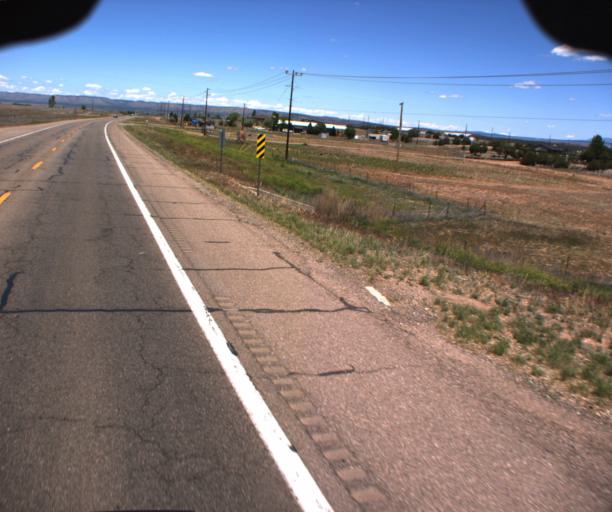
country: US
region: Arizona
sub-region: Yavapai County
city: Paulden
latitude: 34.8428
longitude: -112.4647
